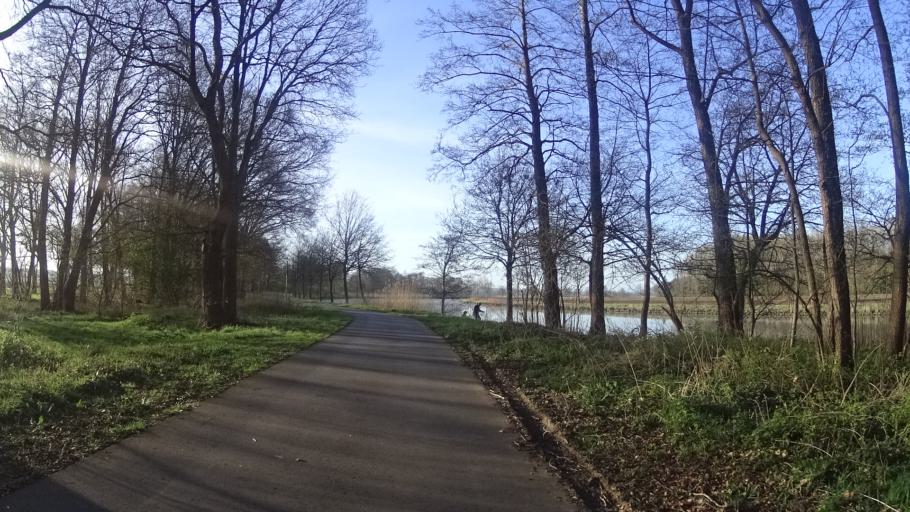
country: DE
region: Lower Saxony
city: Lathen
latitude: 52.8548
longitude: 7.3050
